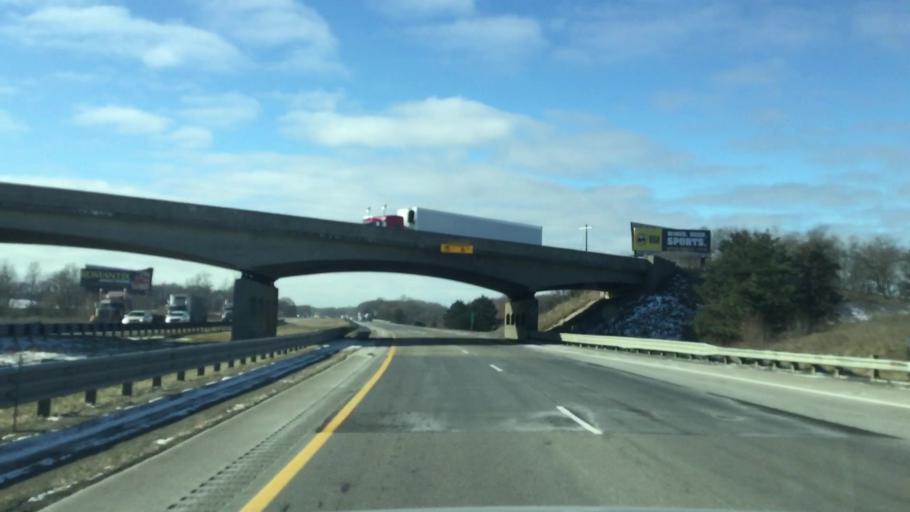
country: US
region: Michigan
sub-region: Calhoun County
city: Brownlee Park
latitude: 42.3000
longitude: -85.0853
